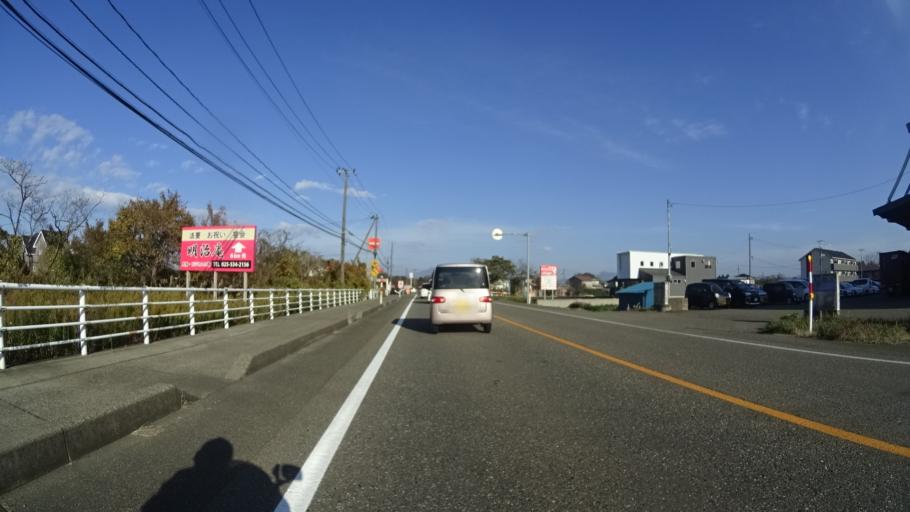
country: JP
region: Niigata
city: Joetsu
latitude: 37.2032
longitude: 138.2970
